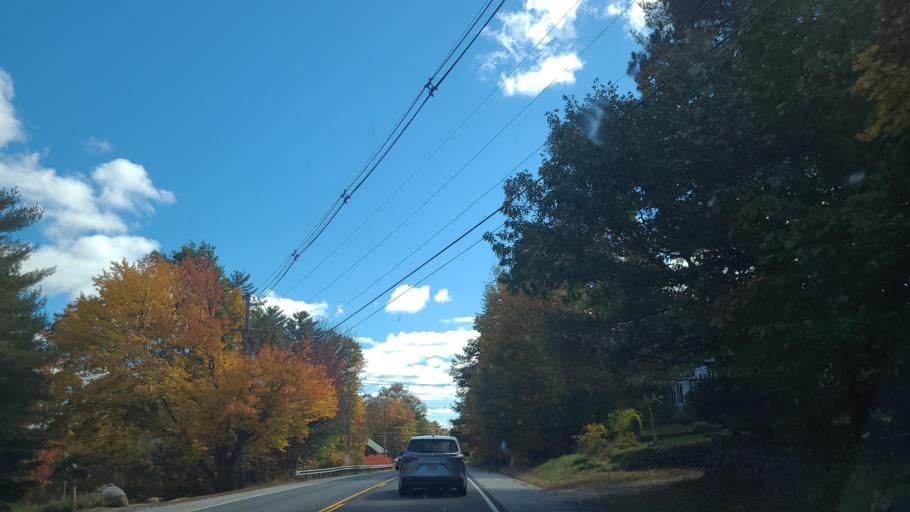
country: US
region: Maine
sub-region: Cumberland County
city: Bridgton
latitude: 43.9802
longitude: -70.6272
